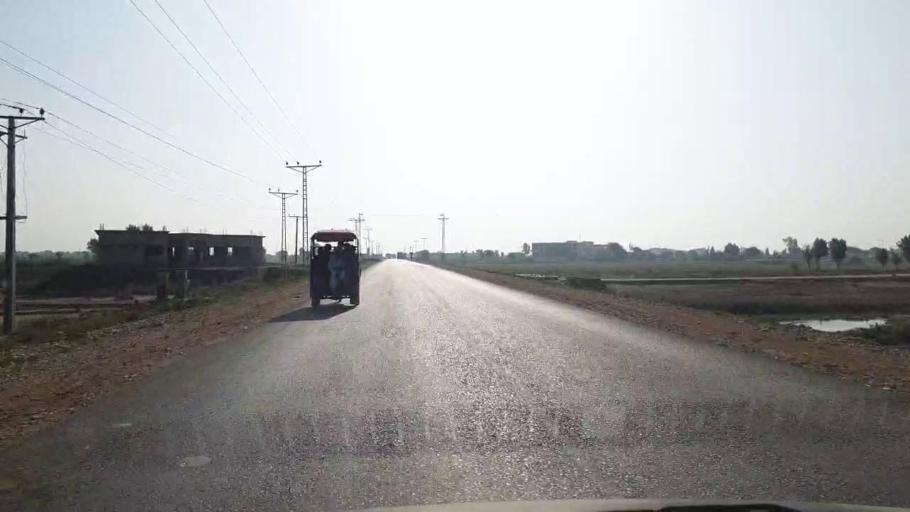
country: PK
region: Sindh
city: Badin
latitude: 24.6686
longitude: 68.8635
